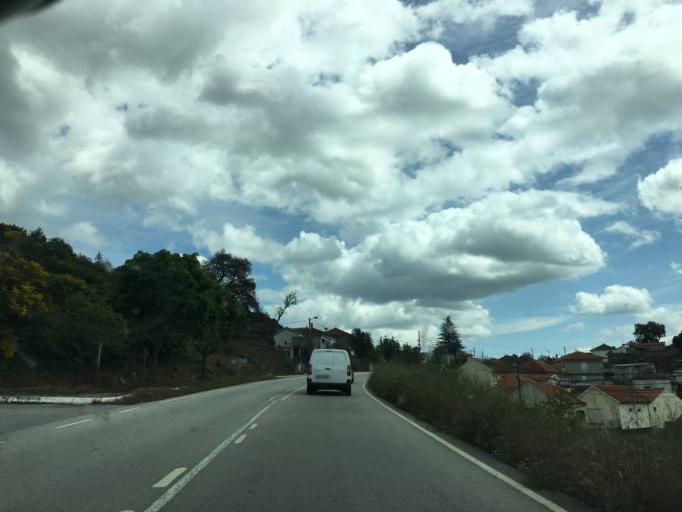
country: PT
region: Vila Real
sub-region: Boticas
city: Boticas
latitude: 41.6949
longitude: -7.6520
